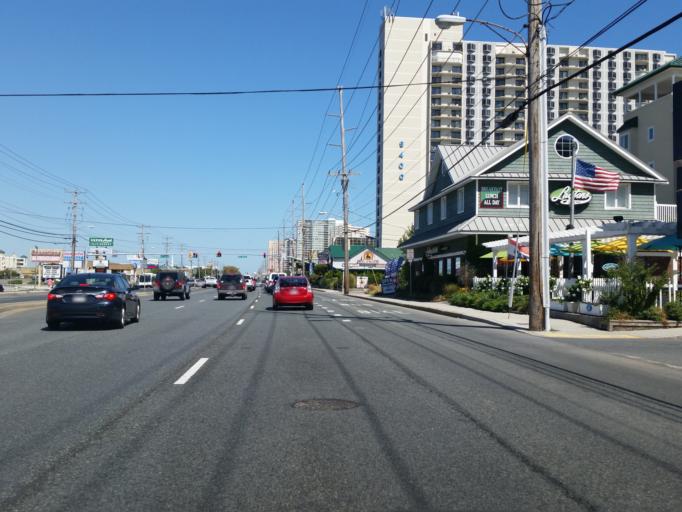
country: US
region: Maryland
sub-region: Worcester County
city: Ocean City
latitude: 38.4079
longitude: -75.0588
